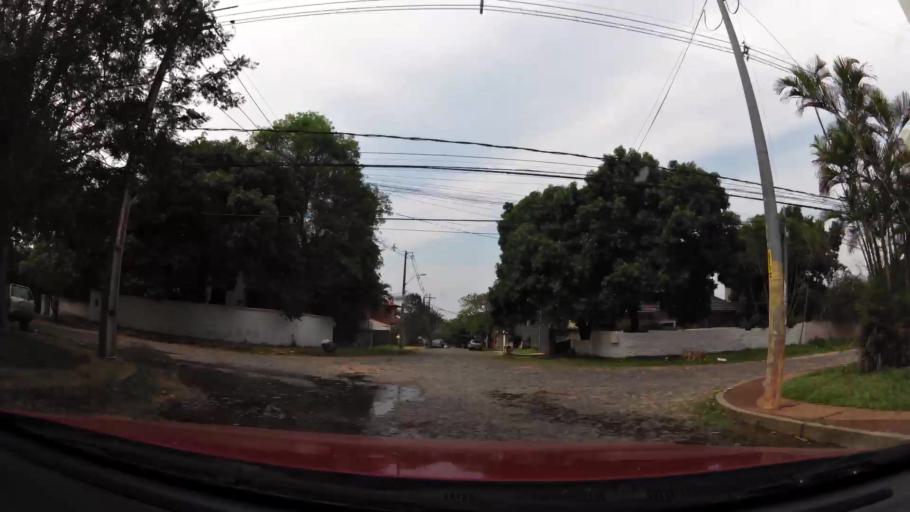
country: PY
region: Asuncion
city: Asuncion
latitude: -25.2754
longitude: -57.5733
